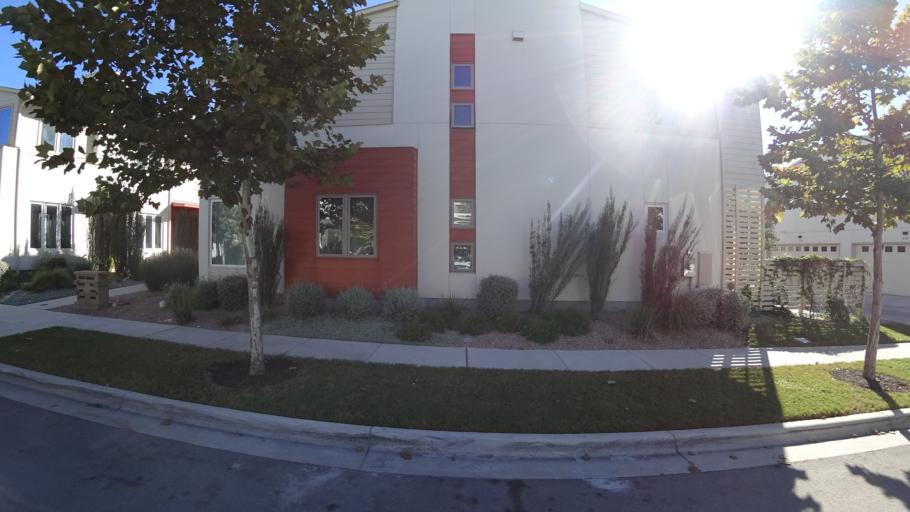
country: US
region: Texas
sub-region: Travis County
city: Austin
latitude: 30.3005
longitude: -97.7013
